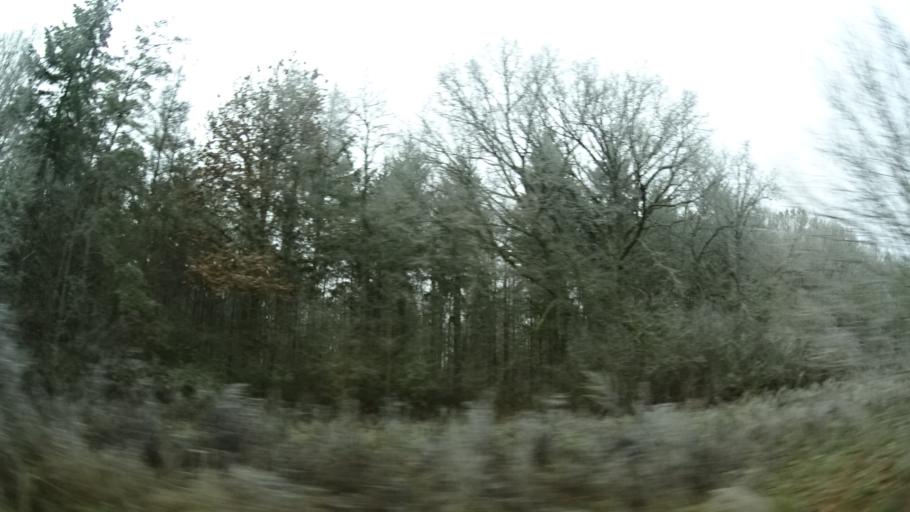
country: DE
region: Baden-Wuerttemberg
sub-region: Karlsruhe Region
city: Osterburken
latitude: 49.4694
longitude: 9.4242
